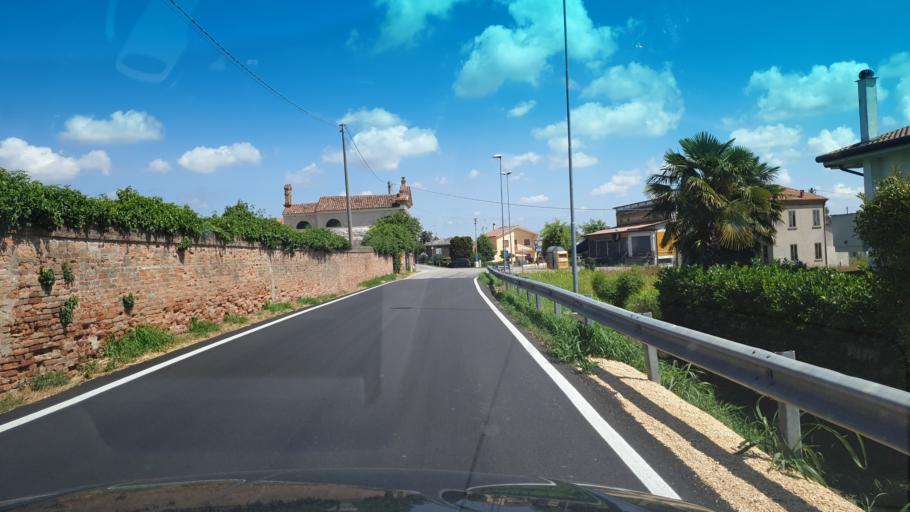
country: IT
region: Veneto
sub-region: Provincia di Rovigo
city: Costa di Rovigo
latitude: 45.0566
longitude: 11.6960
